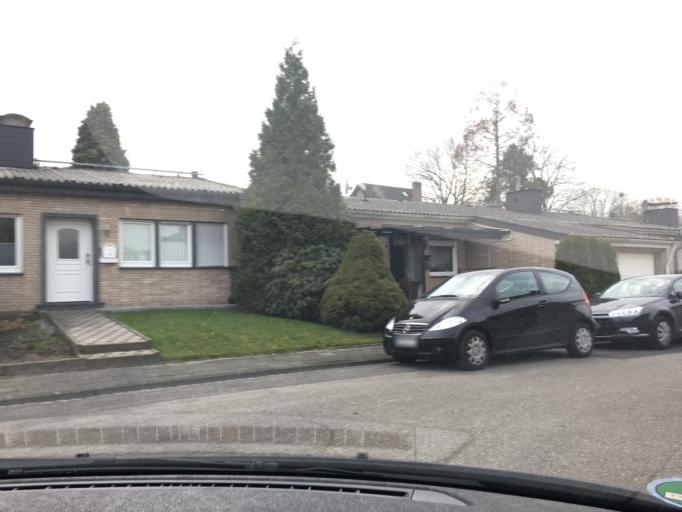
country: DE
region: North Rhine-Westphalia
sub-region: Regierungsbezirk Dusseldorf
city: Monchengladbach
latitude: 51.1332
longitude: 6.4097
